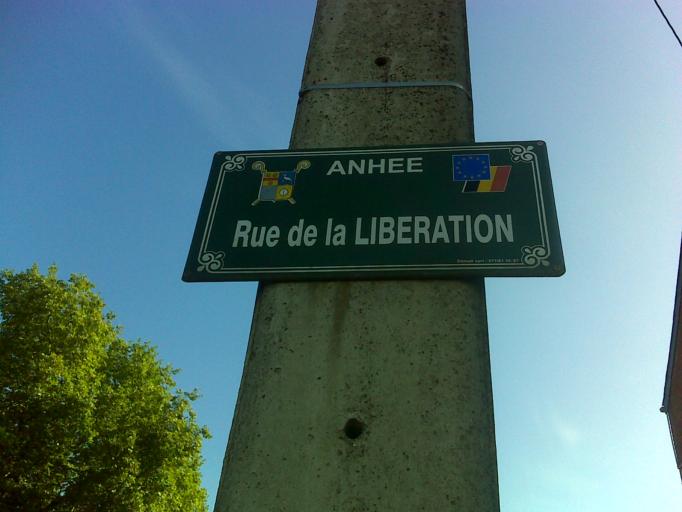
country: BE
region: Wallonia
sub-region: Province de Namur
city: Anhee
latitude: 50.3136
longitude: 4.8763
